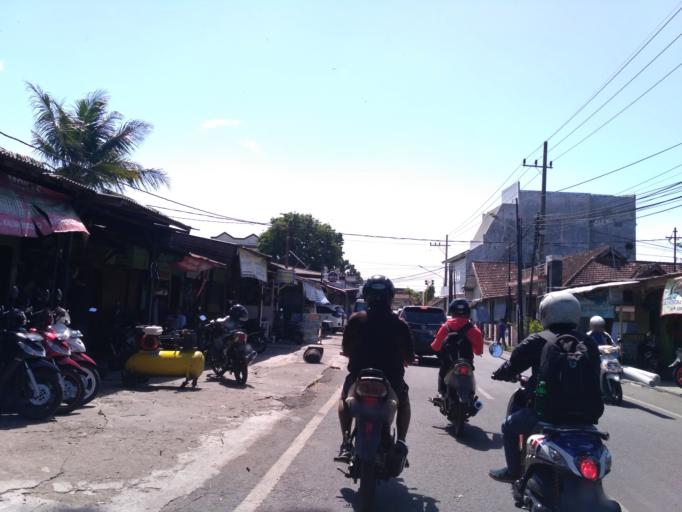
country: ID
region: East Java
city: Malang
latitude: -7.9796
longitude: 112.6490
